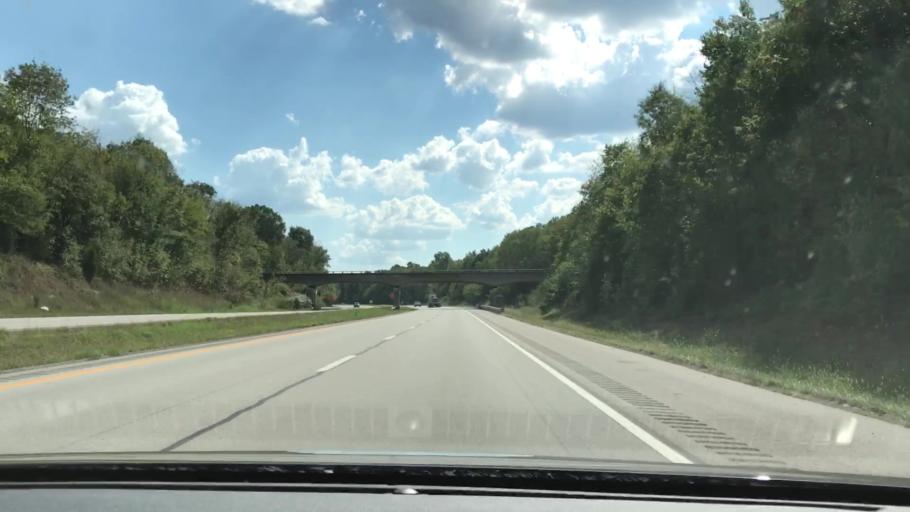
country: US
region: Kentucky
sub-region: Ohio County
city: Oak Grove
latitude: 37.2688
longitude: -86.7478
